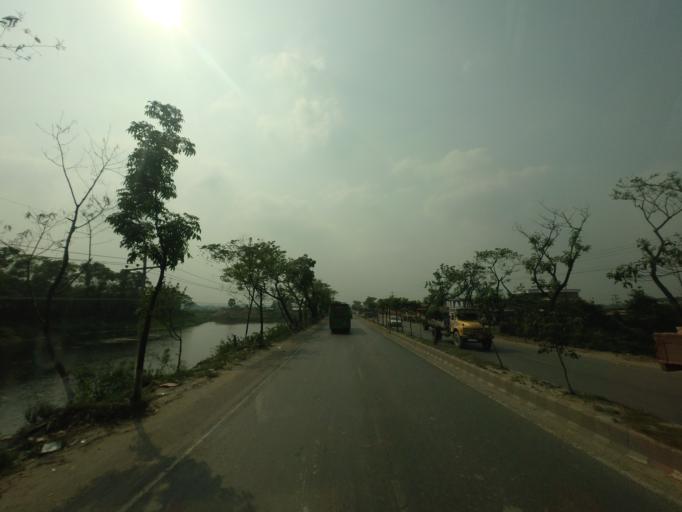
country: BD
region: Dhaka
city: Azimpur
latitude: 23.7927
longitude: 90.3005
